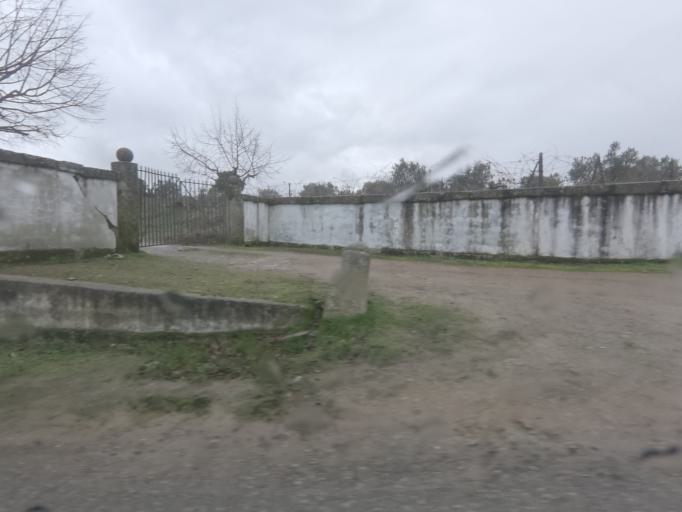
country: PT
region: Viseu
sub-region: Armamar
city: Armamar
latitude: 41.1613
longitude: -7.7104
